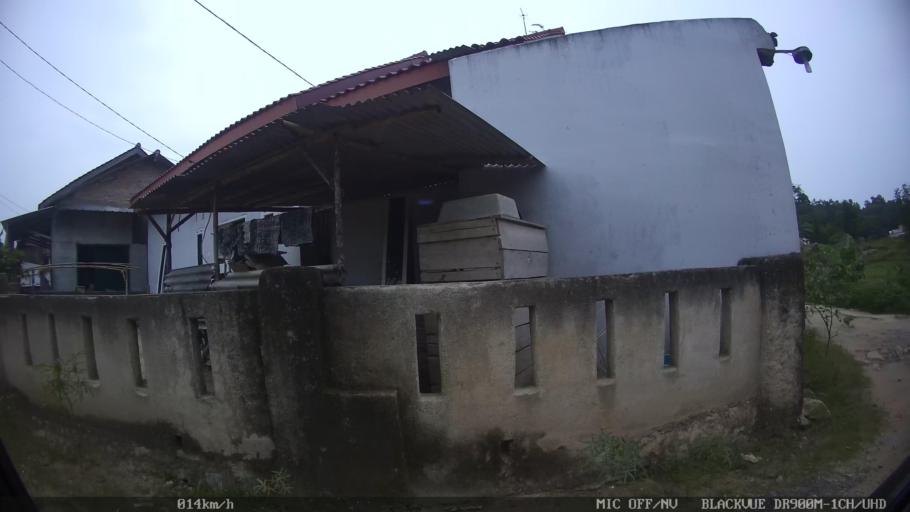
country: ID
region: Lampung
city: Panjang
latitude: -5.4270
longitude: 105.3417
